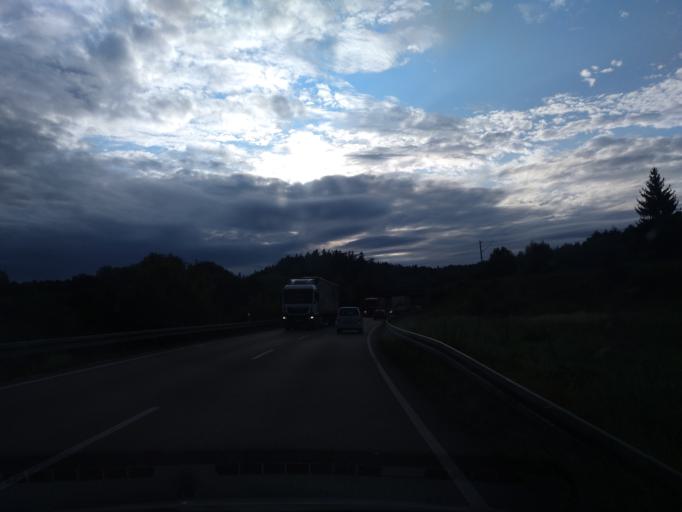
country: DE
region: Bavaria
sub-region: Upper Bavaria
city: Oberhausen
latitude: 48.7163
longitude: 11.0799
